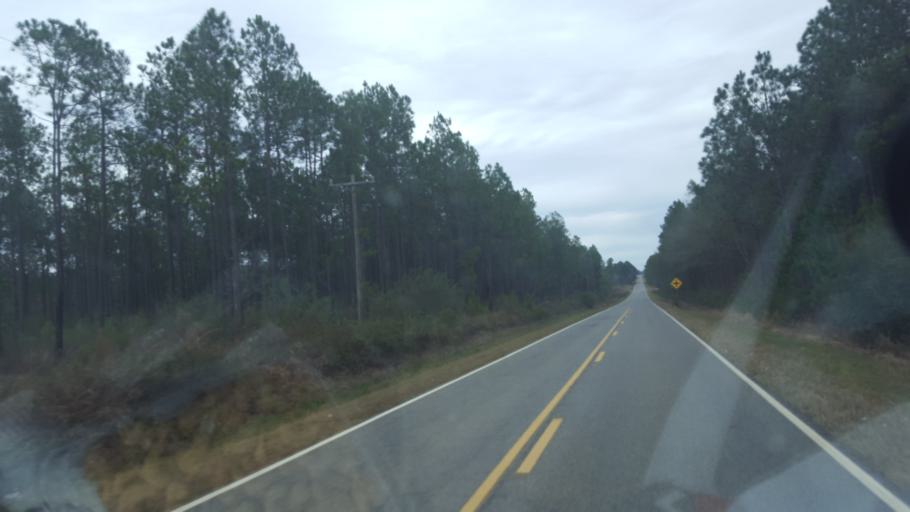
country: US
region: Georgia
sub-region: Ben Hill County
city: Fitzgerald
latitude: 31.7830
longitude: -83.4111
